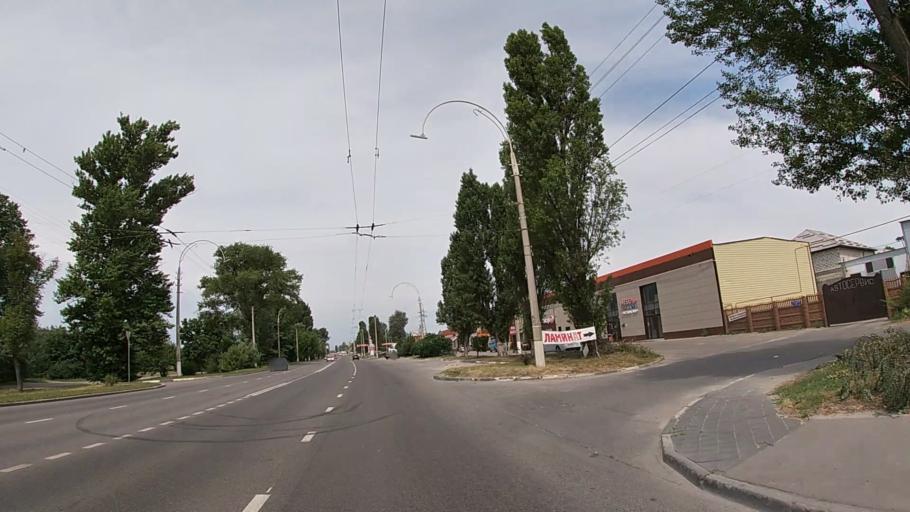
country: RU
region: Belgorod
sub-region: Belgorodskiy Rayon
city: Belgorod
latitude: 50.6096
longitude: 36.5452
